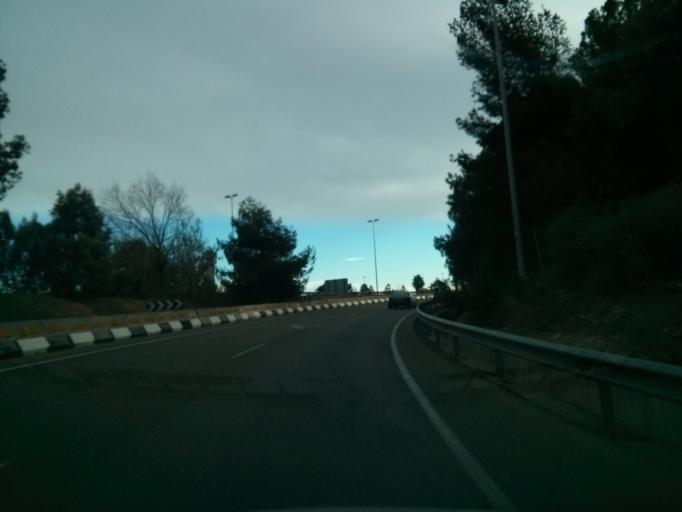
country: ES
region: Valencia
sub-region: Provincia de Valencia
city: Paterna
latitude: 39.5102
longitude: -0.4278
